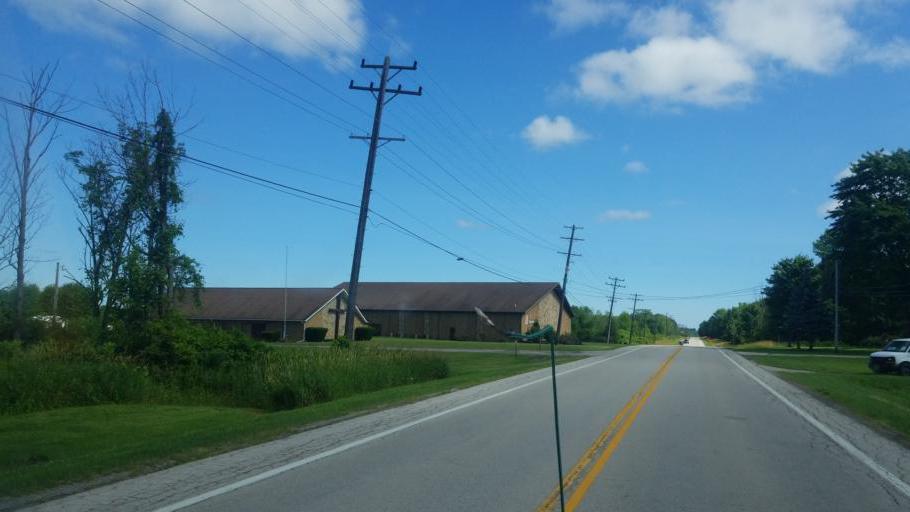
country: US
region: Ohio
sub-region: Ashtabula County
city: Conneaut
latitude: 41.8714
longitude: -80.5723
